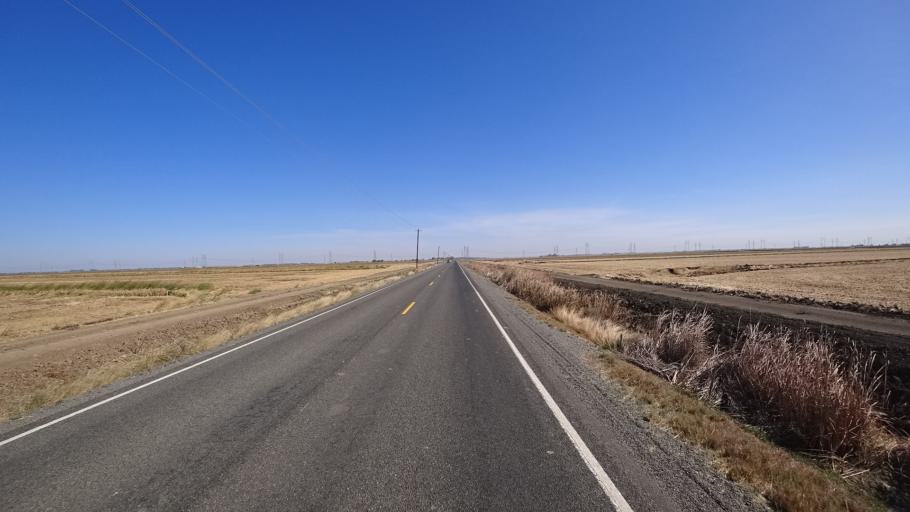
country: US
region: California
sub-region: Yolo County
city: Cottonwood
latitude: 38.6203
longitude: -121.9450
